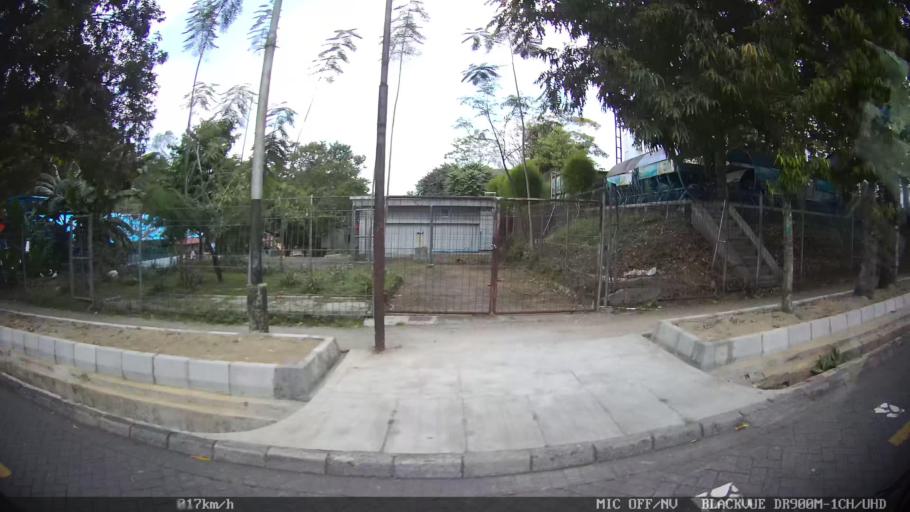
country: ID
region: Daerah Istimewa Yogyakarta
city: Yogyakarta
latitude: -7.7670
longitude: 110.3823
